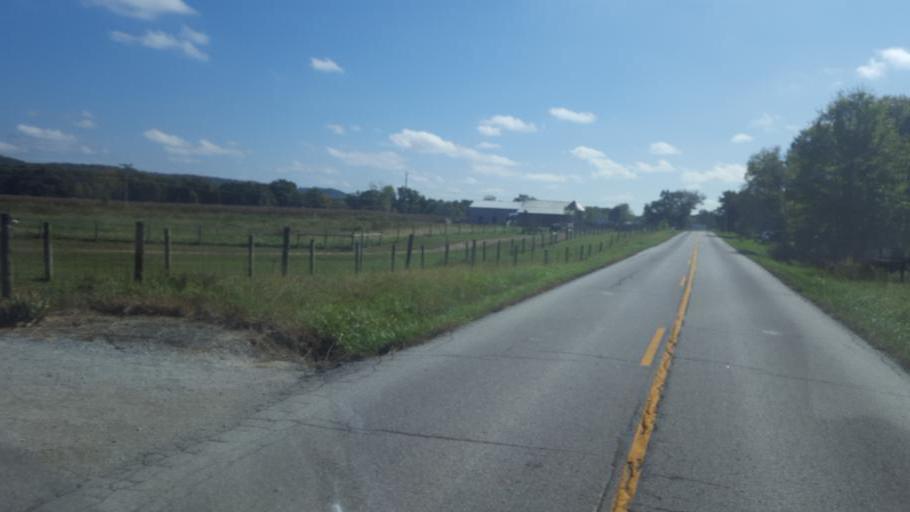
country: US
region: Kentucky
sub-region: Fleming County
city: Flemingsburg
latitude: 38.4820
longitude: -83.6088
